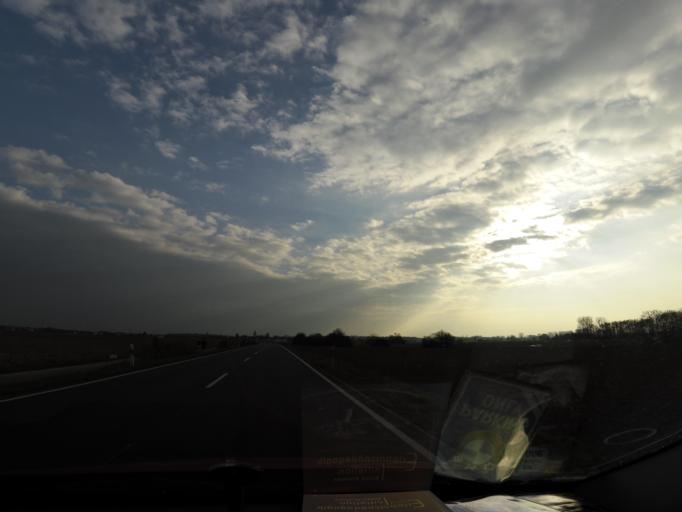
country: DE
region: Baden-Wuerttemberg
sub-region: Freiburg Region
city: Rheinau
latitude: 48.6346
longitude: 7.9026
